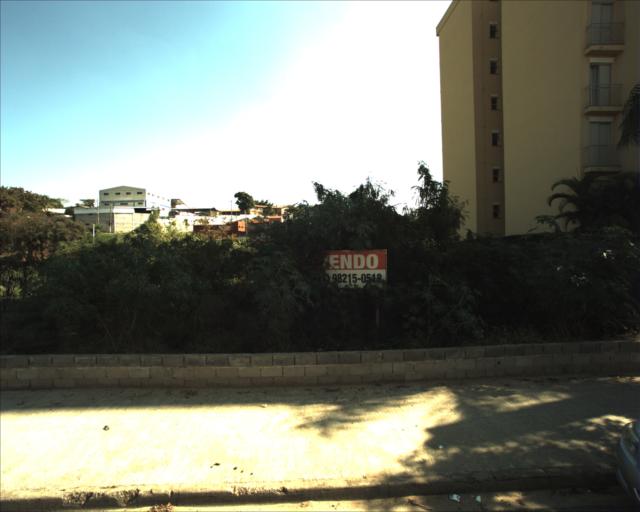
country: BR
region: Sao Paulo
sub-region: Sorocaba
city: Sorocaba
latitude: -23.4953
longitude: -47.4299
